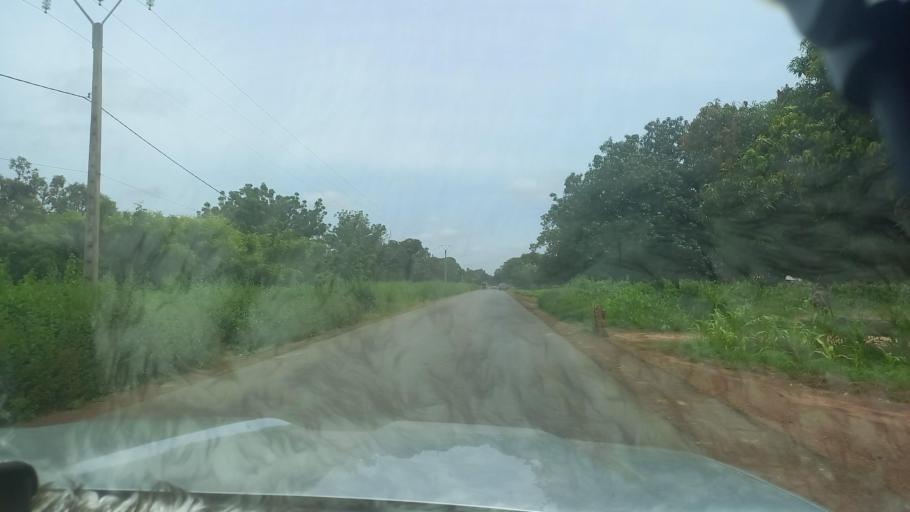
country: SN
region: Kolda
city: Marsassoum
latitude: 12.9636
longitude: -15.9773
